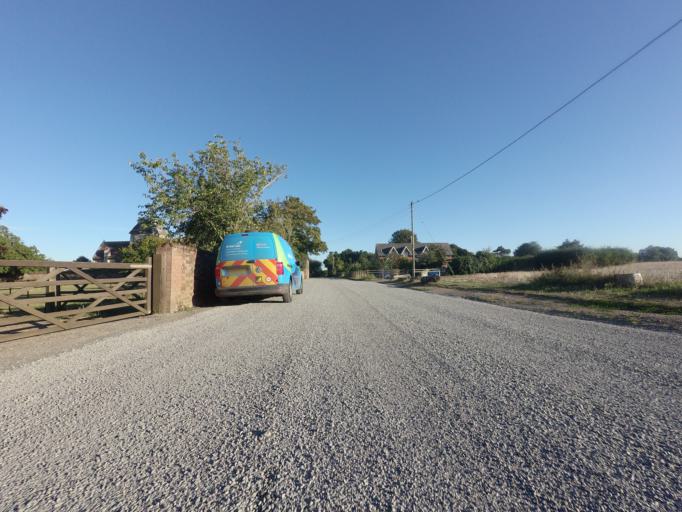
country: GB
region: England
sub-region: Kent
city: Herne Bay
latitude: 51.3350
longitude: 1.1911
